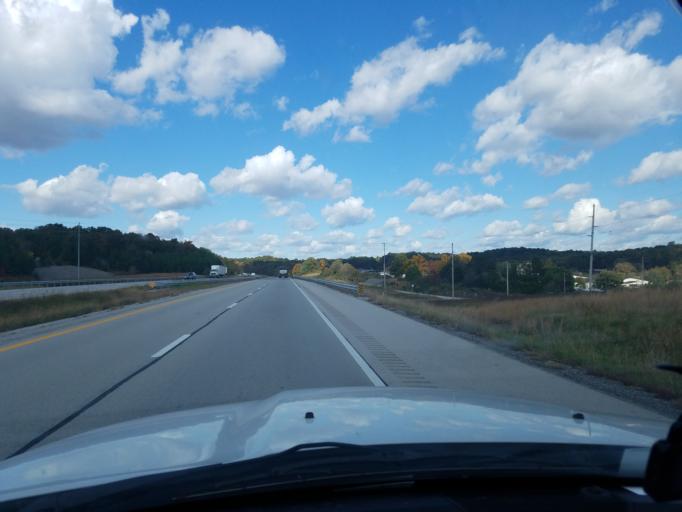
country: US
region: Kentucky
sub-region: Butler County
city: Morgantown
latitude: 37.2135
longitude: -86.7103
